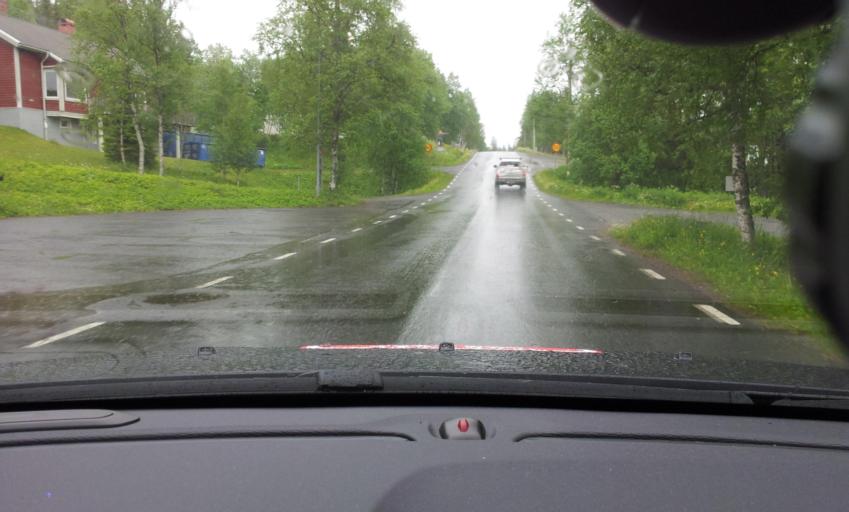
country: SE
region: Jaemtland
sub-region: Are Kommun
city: Are
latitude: 63.3152
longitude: 13.0882
